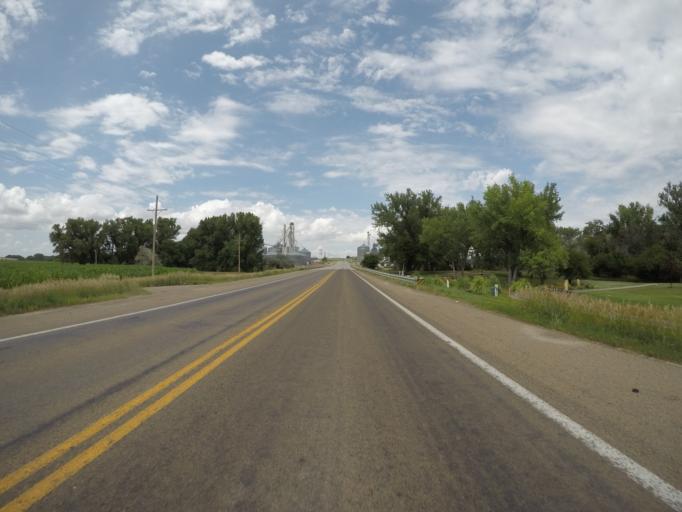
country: US
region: Kansas
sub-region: Rawlins County
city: Atwood
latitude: 39.8203
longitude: -101.0468
